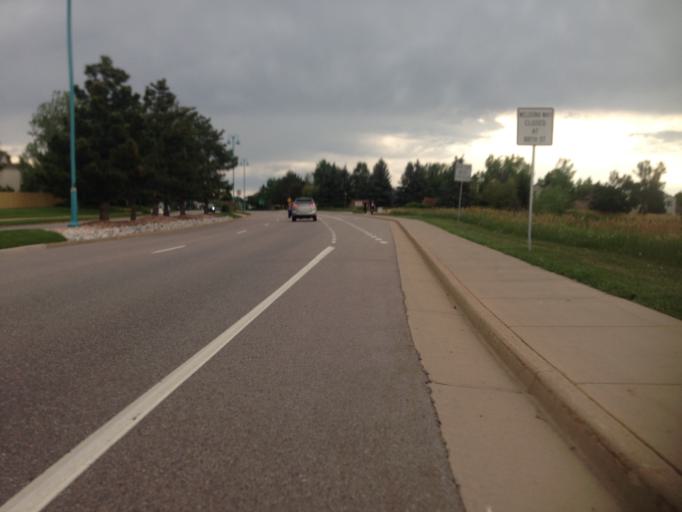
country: US
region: Colorado
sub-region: Boulder County
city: Superior
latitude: 39.9356
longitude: -105.1459
